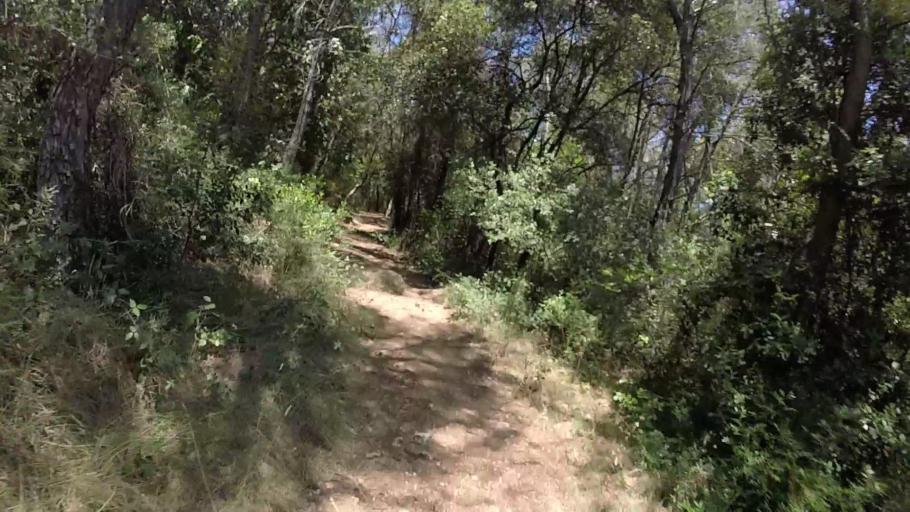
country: FR
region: Provence-Alpes-Cote d'Azur
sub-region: Departement des Alpes-Maritimes
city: Vallauris
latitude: 43.5980
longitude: 7.0374
